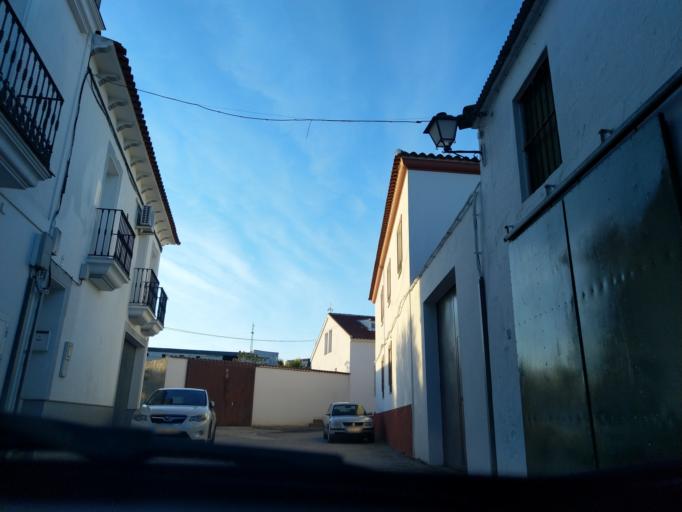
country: ES
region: Extremadura
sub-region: Provincia de Badajoz
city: Valverde de Llerena
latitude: 38.2142
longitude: -5.8238
